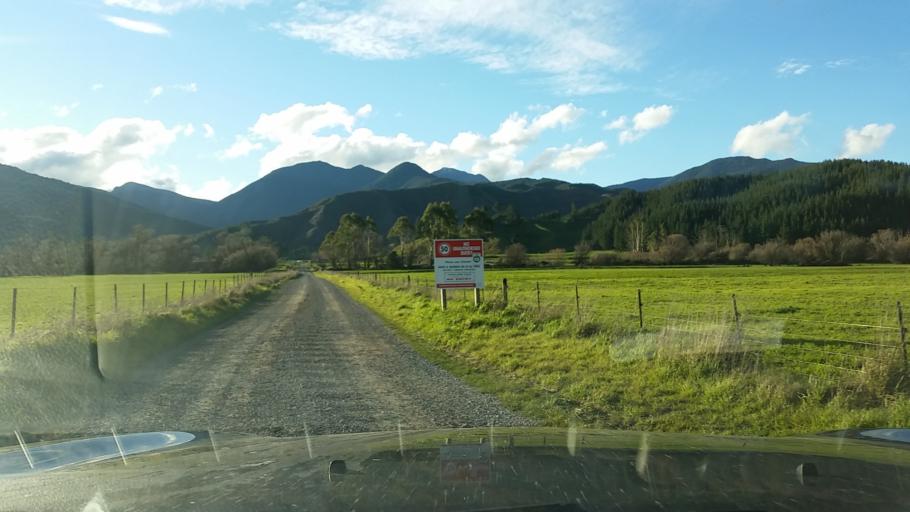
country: NZ
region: Nelson
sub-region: Nelson City
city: Nelson
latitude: -41.5474
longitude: 173.4987
